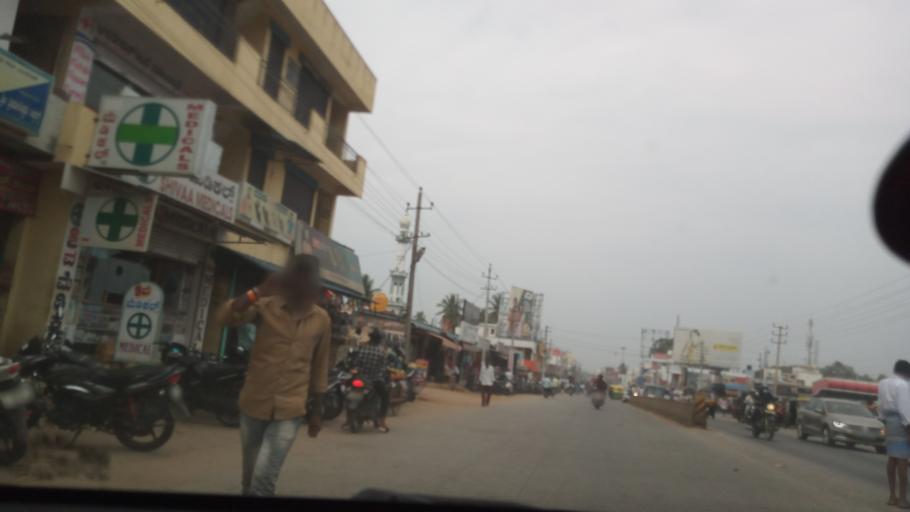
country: IN
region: Karnataka
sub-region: Chamrajnagar
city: Chamrajnagar
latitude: 11.9237
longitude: 76.9399
